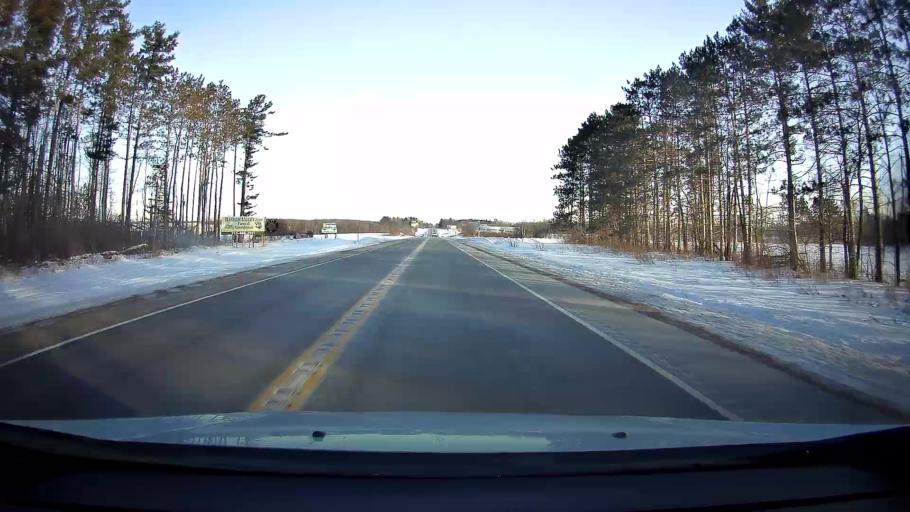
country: US
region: Wisconsin
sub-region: Washburn County
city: Shell Lake
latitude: 45.7635
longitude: -91.9128
